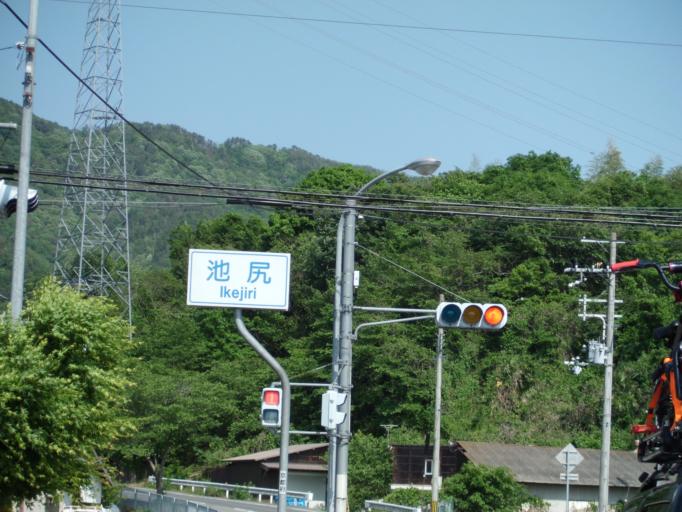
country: JP
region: Kyoto
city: Kameoka
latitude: 35.0643
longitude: 135.5639
